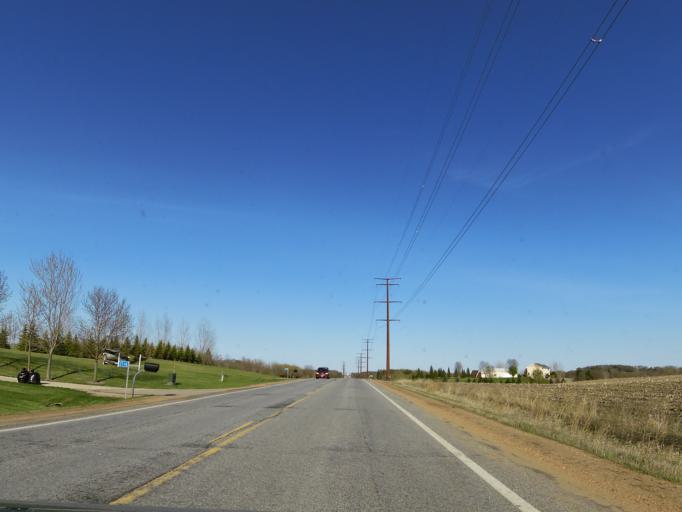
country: US
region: Minnesota
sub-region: Le Sueur County
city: New Prague
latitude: 44.5725
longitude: -93.4793
